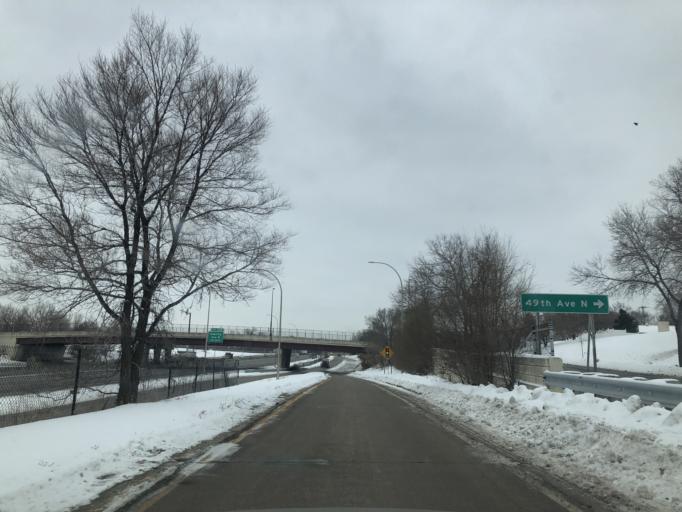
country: US
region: Minnesota
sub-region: Anoka County
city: Columbia Heights
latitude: 45.0452
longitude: -93.2852
